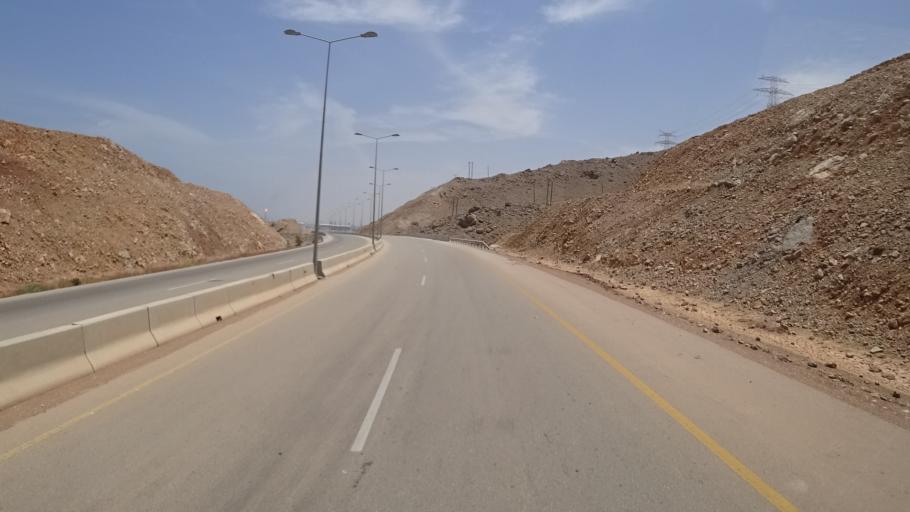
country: OM
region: Ash Sharqiyah
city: Sur
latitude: 22.6815
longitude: 59.3803
